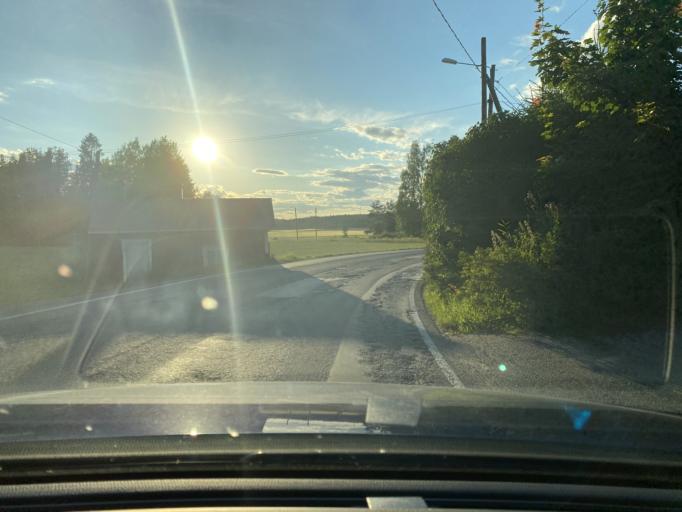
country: FI
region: Uusimaa
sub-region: Helsinki
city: Nurmijaervi
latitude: 60.3947
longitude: 24.8045
